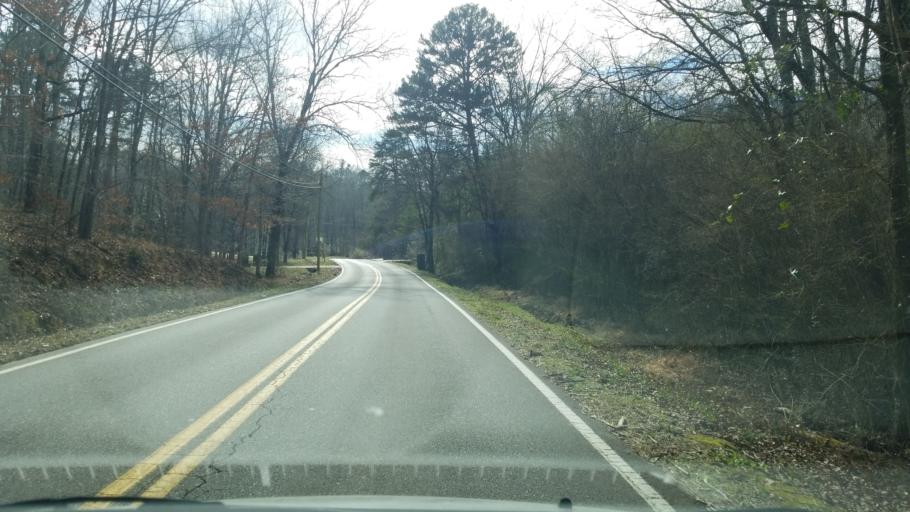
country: US
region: Tennessee
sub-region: Hamilton County
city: Collegedale
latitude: 35.0470
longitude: -85.1105
